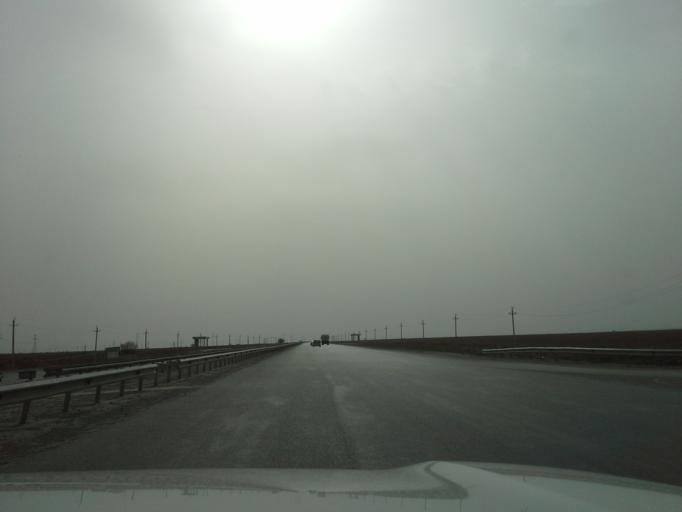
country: IR
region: Razavi Khorasan
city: Dargaz
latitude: 37.5570
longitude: 59.3669
